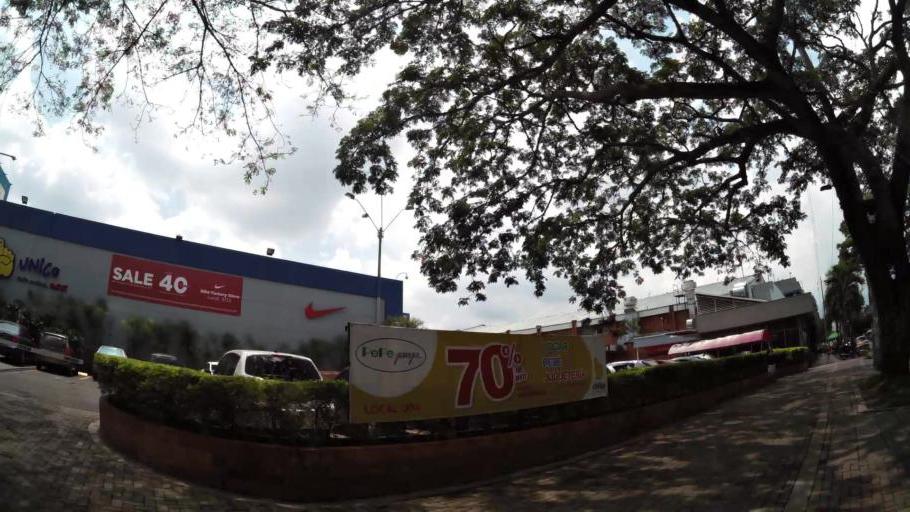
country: CO
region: Valle del Cauca
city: Cali
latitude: 3.4657
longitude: -76.5006
